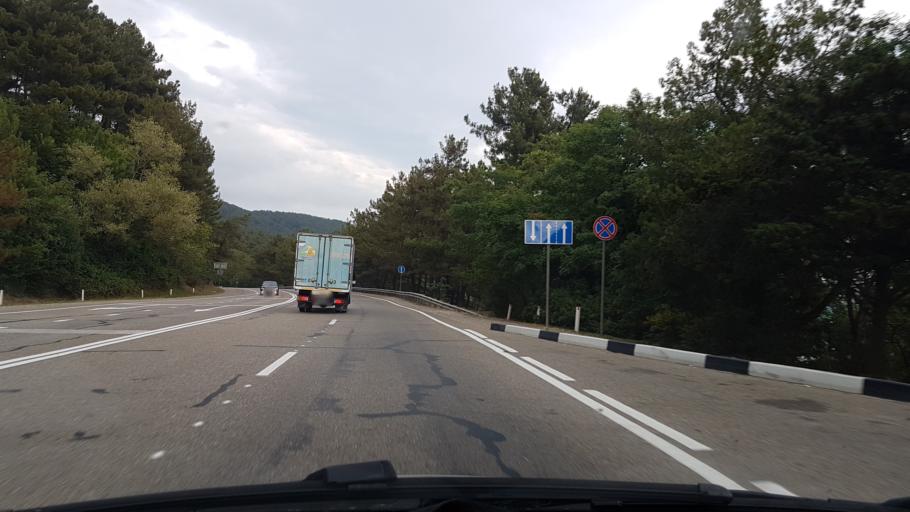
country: RU
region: Krasnodarskiy
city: Ol'ginka
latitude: 44.1864
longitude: 38.9025
